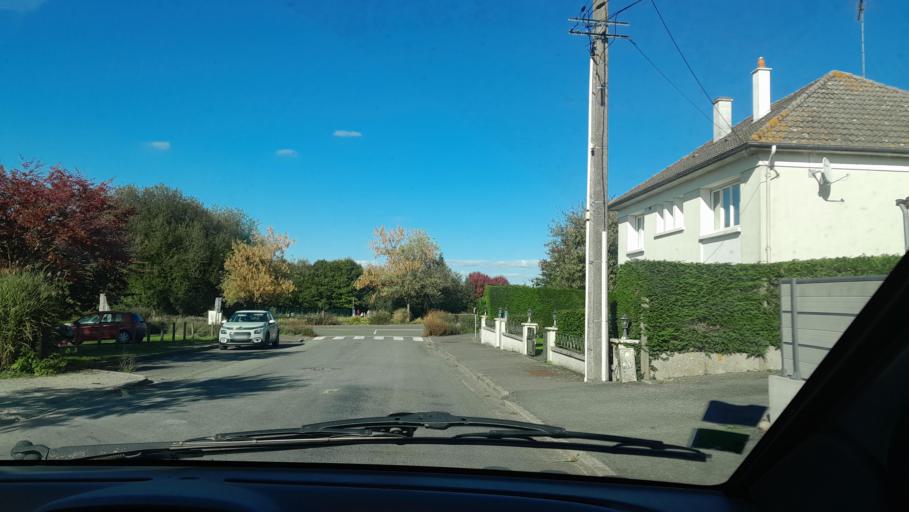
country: FR
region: Pays de la Loire
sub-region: Departement de la Mayenne
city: Quelaines-Saint-Gault
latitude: 47.9250
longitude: -0.8066
